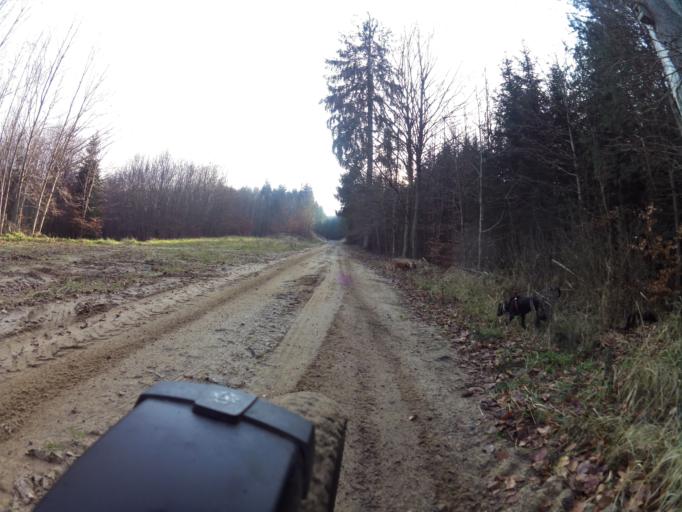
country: PL
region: West Pomeranian Voivodeship
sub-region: Powiat koszalinski
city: Polanow
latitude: 54.1799
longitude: 16.7207
